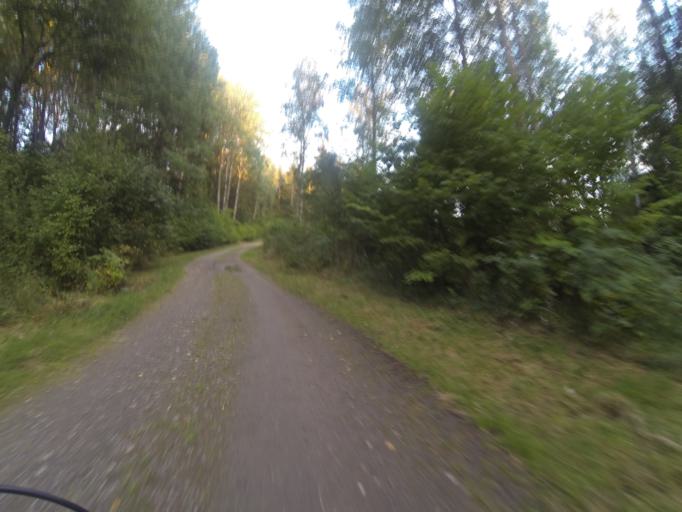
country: SE
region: Soedermanland
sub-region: Eskilstuna Kommun
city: Kvicksund
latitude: 59.4498
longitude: 16.3884
